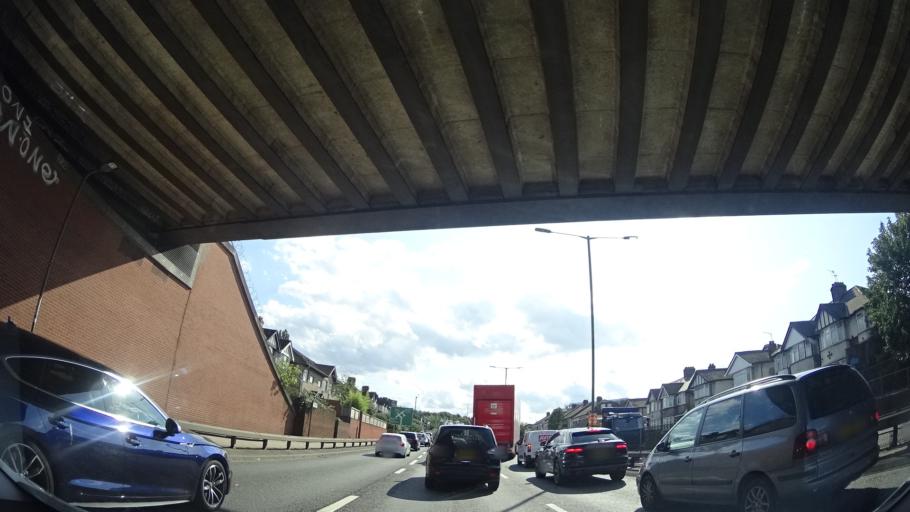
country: GB
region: England
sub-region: Greater London
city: Ealing Broadway
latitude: 51.5329
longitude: -0.2912
